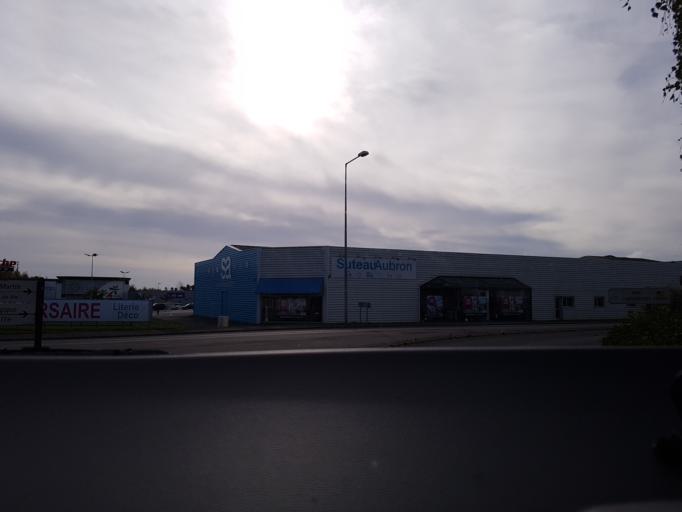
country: FR
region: Pays de la Loire
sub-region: Departement de Maine-et-Loire
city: Beaupreau
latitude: 47.2057
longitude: -0.9758
